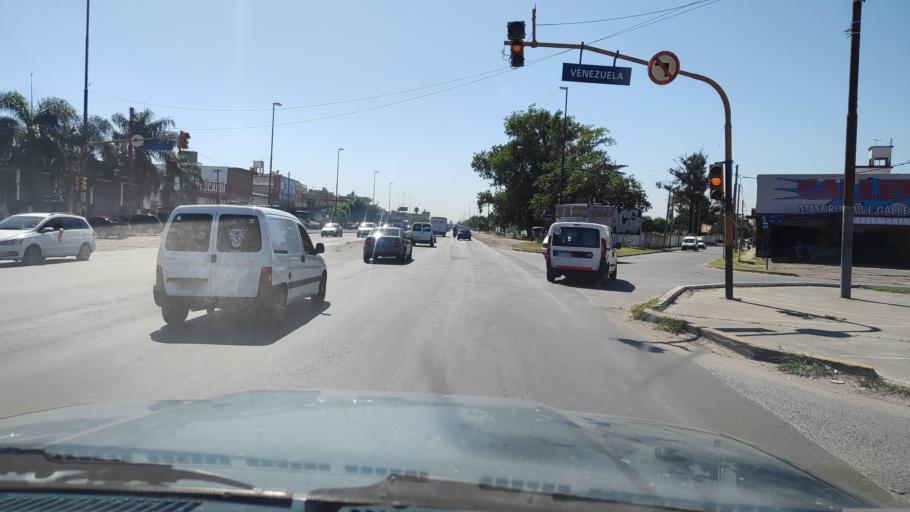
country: AR
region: Buenos Aires
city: San Justo
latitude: -34.6797
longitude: -58.5841
